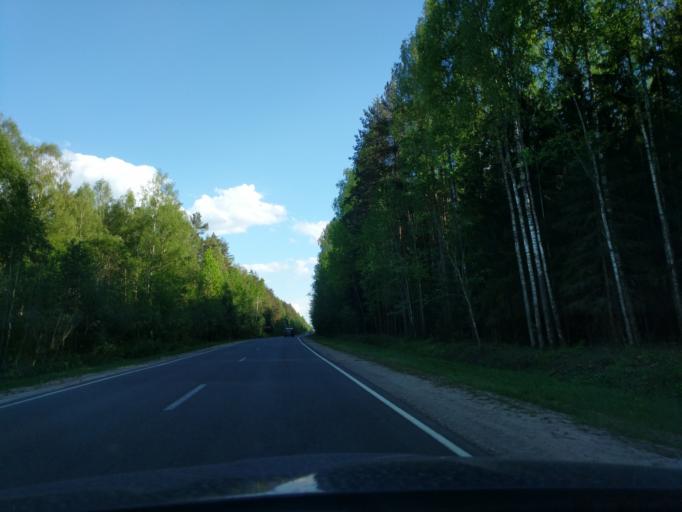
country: BY
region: Minsk
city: Kryvichy
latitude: 54.5977
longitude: 27.1884
